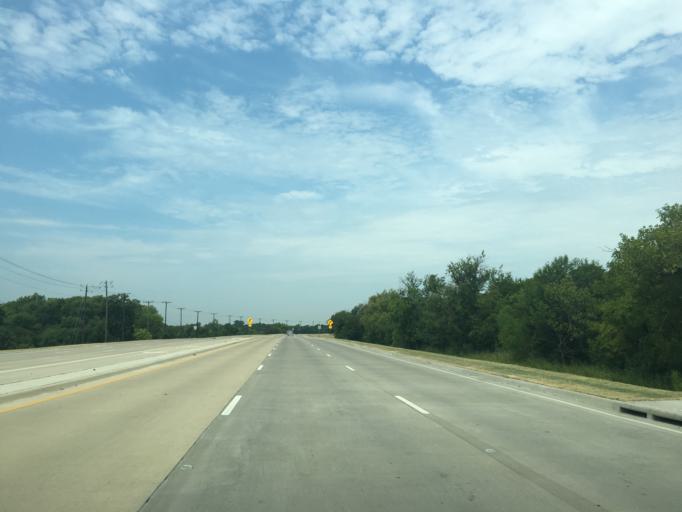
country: US
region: Texas
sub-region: Collin County
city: Lavon
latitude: 33.0219
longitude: -96.4655
